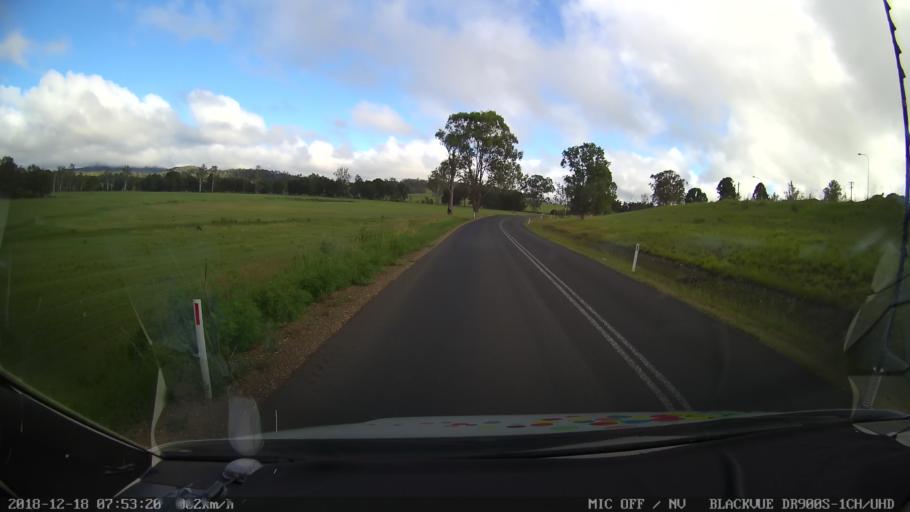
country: AU
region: New South Wales
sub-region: Kyogle
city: Kyogle
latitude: -28.4204
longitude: 152.5828
